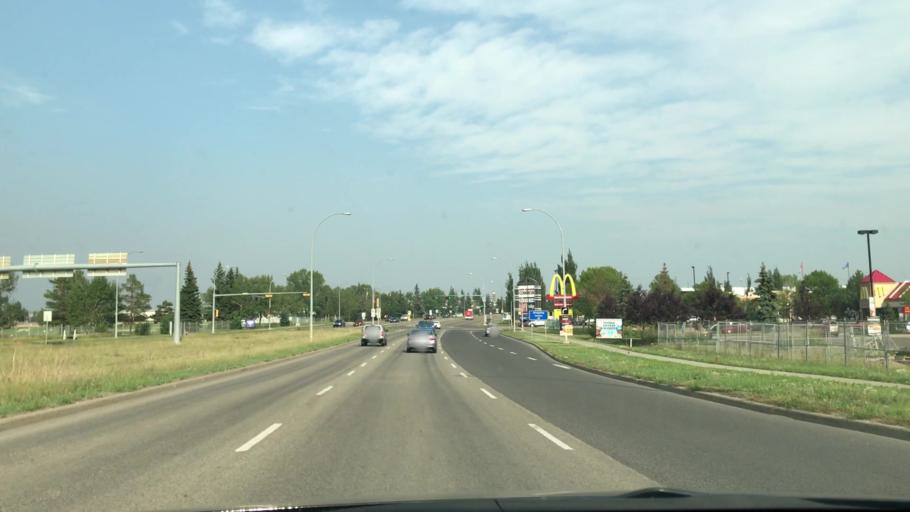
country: CA
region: Alberta
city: Edmonton
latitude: 53.4538
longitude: -113.4886
